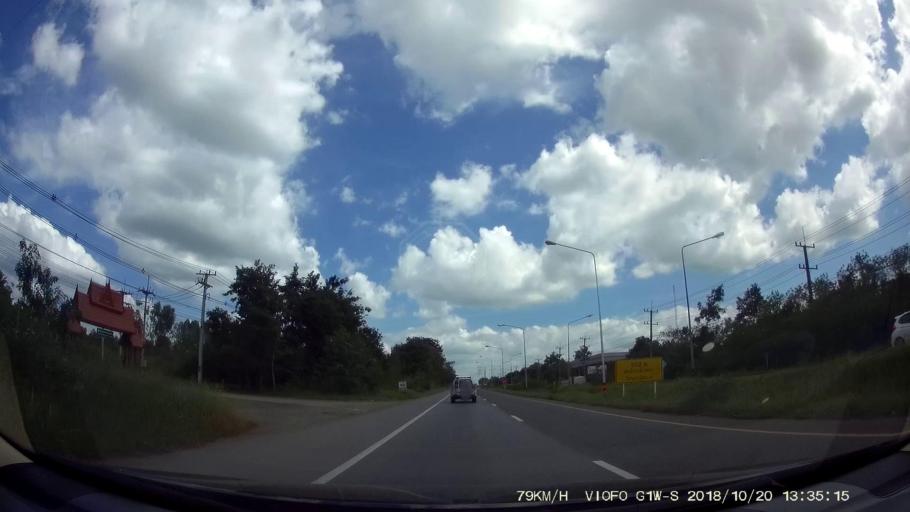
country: TH
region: Khon Kaen
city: Chum Phae
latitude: 16.5695
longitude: 102.0445
